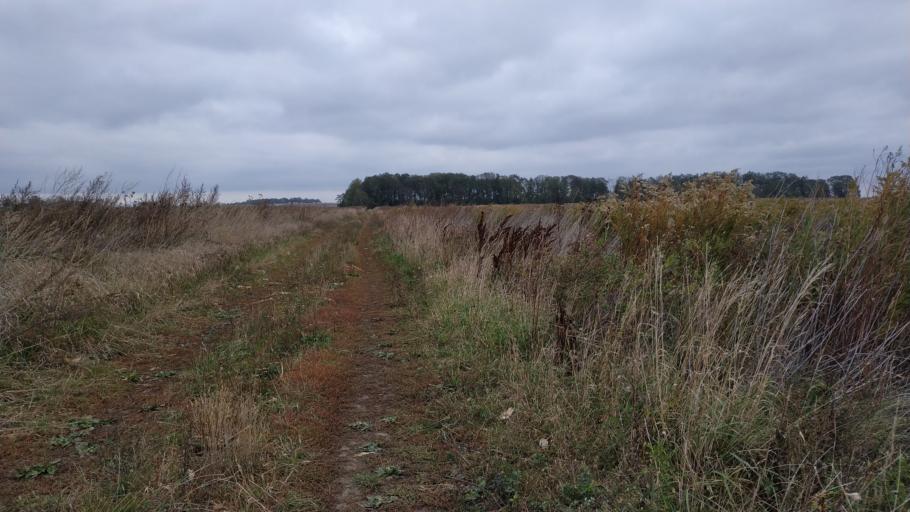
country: PL
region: Lower Silesian Voivodeship
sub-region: Powiat wroclawski
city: Tyniec Maly
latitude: 51.0247
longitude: 16.9433
